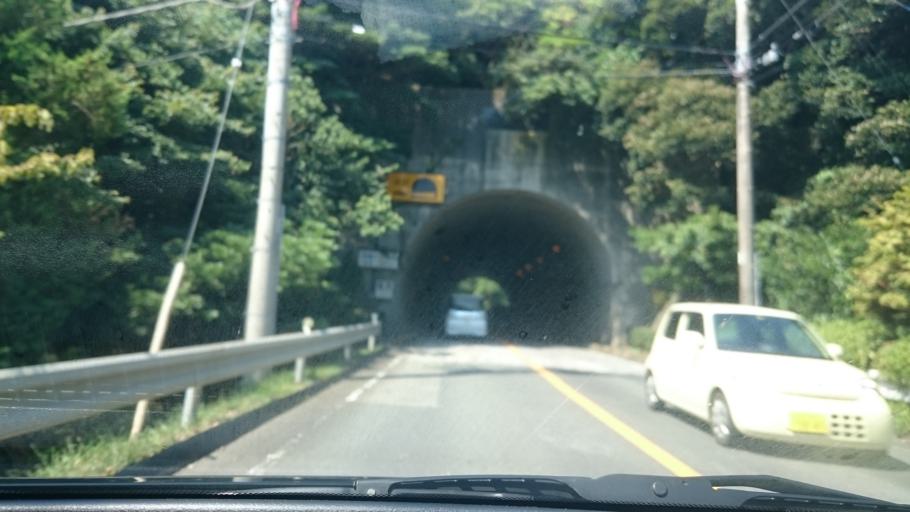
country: JP
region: Shizuoka
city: Heda
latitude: 34.7933
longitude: 138.7641
